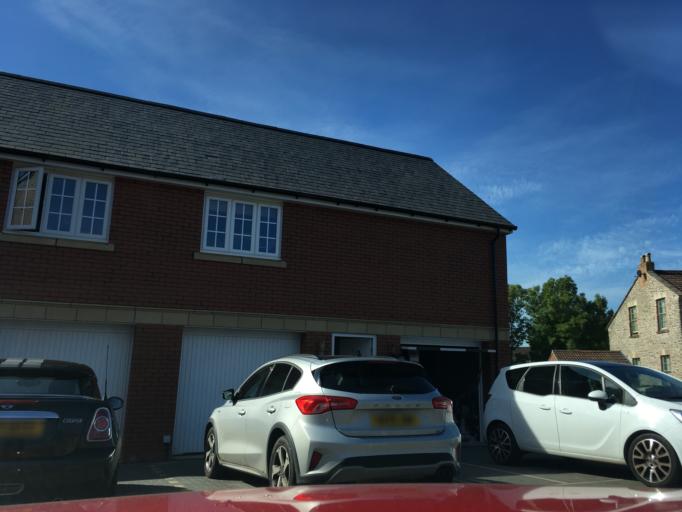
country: GB
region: England
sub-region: South Gloucestershire
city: Bitton
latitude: 51.4258
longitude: -2.4597
